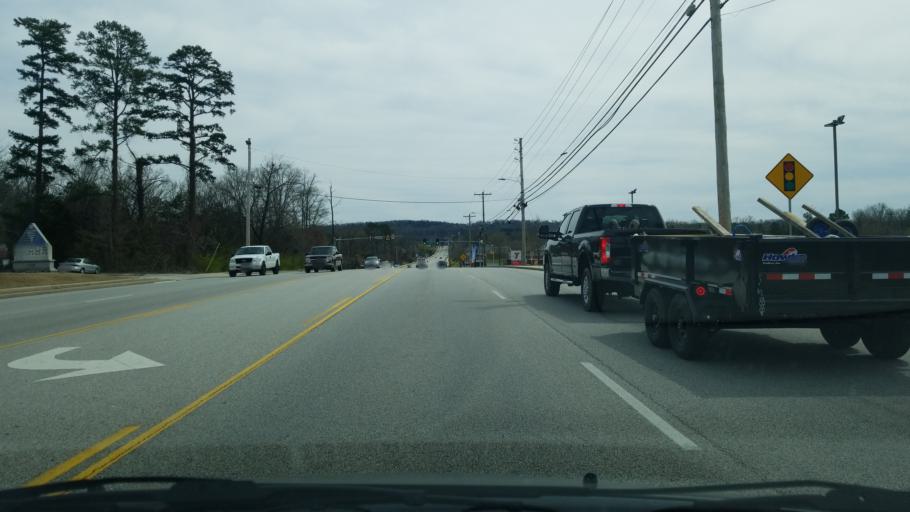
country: US
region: Tennessee
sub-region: Hamilton County
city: East Brainerd
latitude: 35.0394
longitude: -85.1476
